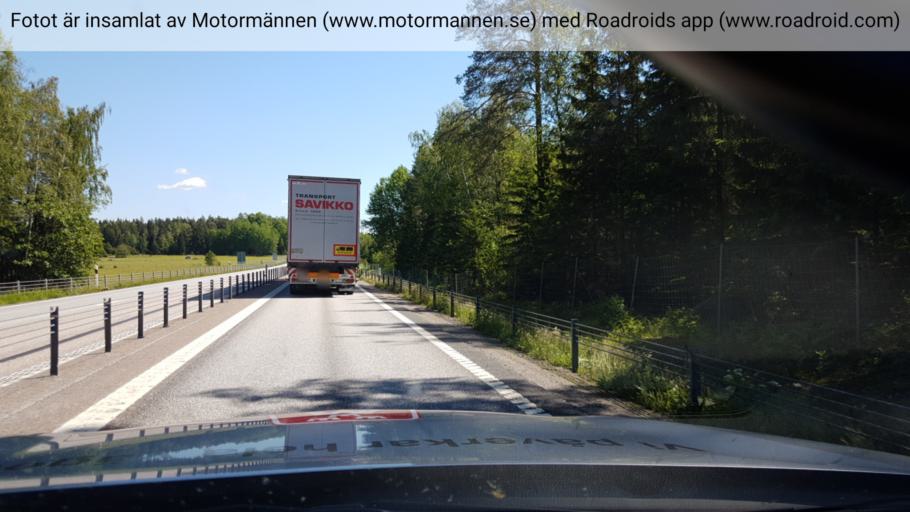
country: SE
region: Vaestmanland
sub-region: Hallstahammars Kommun
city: Hallstahammar
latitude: 59.5799
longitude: 16.1444
